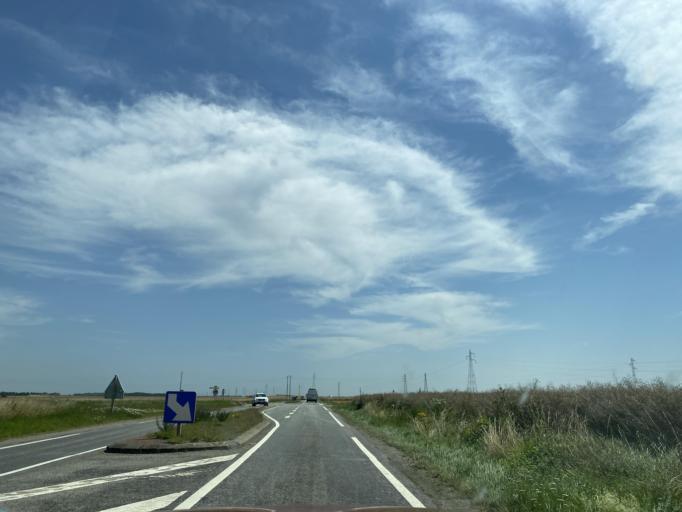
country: FR
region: Centre
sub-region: Departement d'Eure-et-Loir
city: Le Coudray
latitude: 48.4125
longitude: 1.5073
